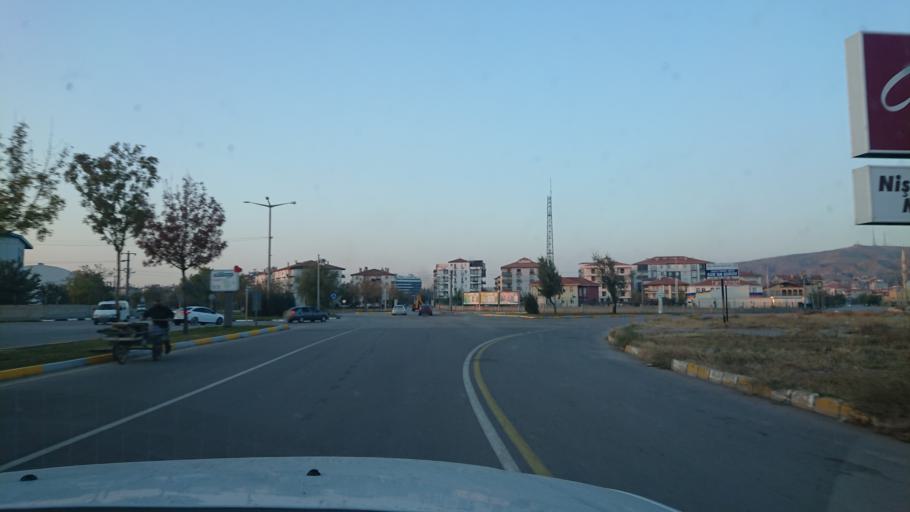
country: TR
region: Aksaray
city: Aksaray
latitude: 38.3518
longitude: 34.0429
